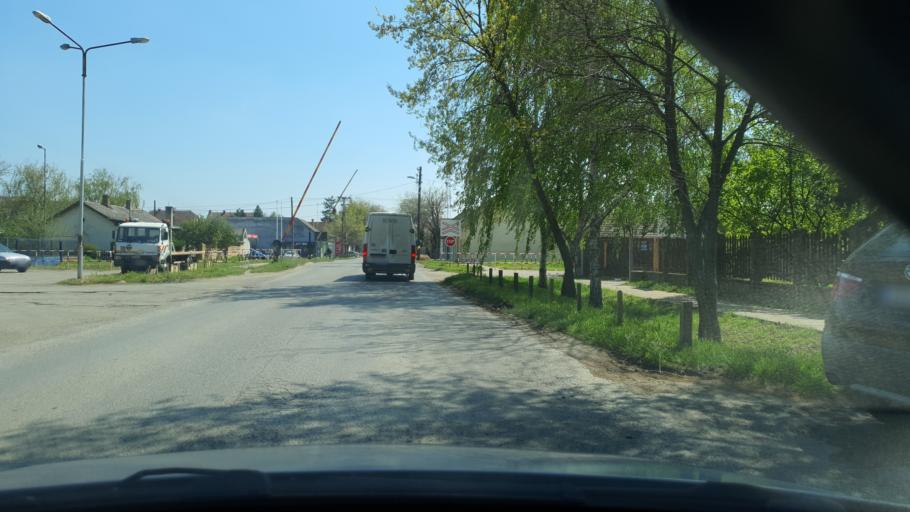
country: RS
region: Autonomna Pokrajina Vojvodina
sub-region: Zapadnobacki Okrug
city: Odzaci
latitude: 45.5104
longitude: 19.2537
